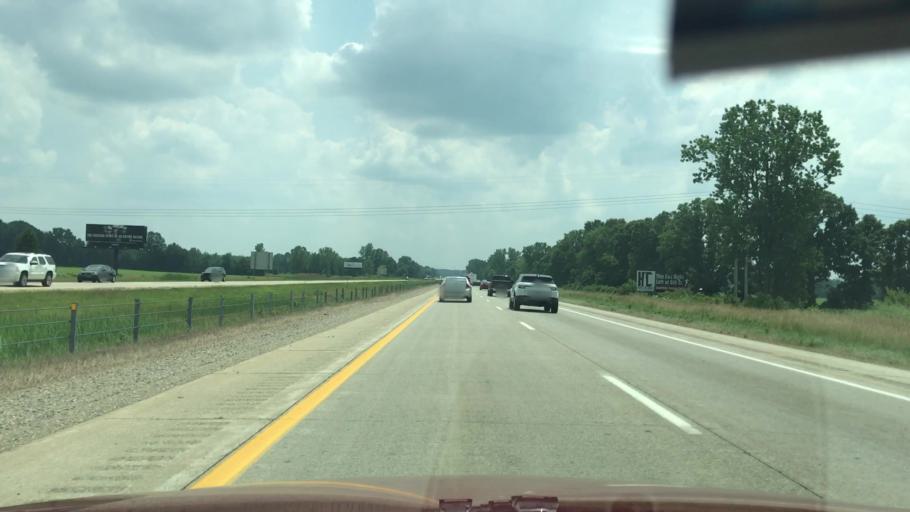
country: US
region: Michigan
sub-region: Allegan County
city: Plainwell
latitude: 42.4297
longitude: -85.6610
